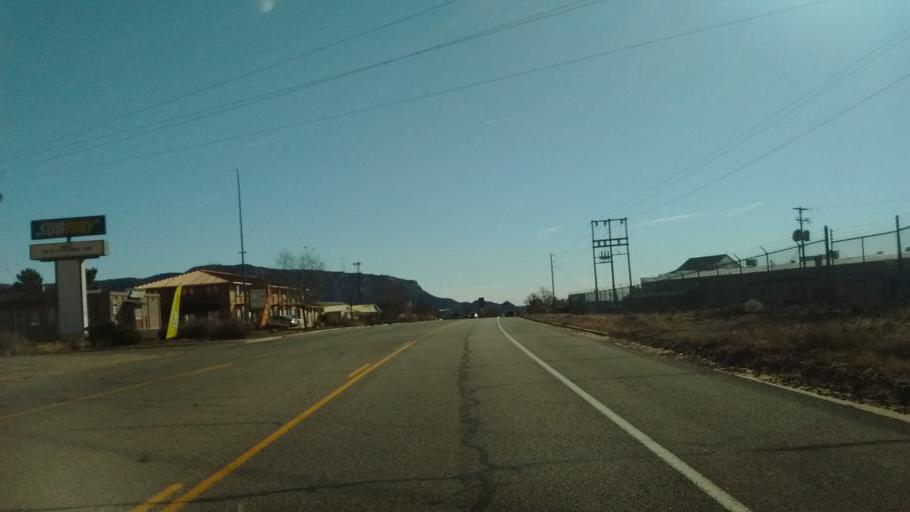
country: US
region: Arizona
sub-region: Mohave County
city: Colorado City
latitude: 37.0036
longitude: -113.0022
